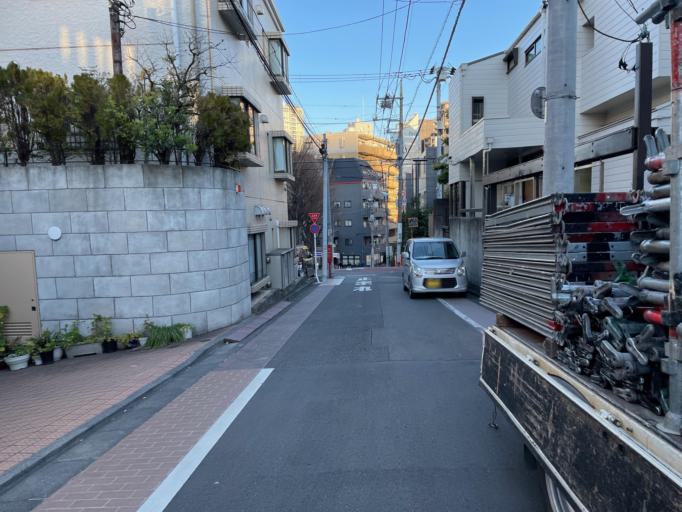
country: JP
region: Tokyo
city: Tokyo
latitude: 35.6298
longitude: 139.7246
